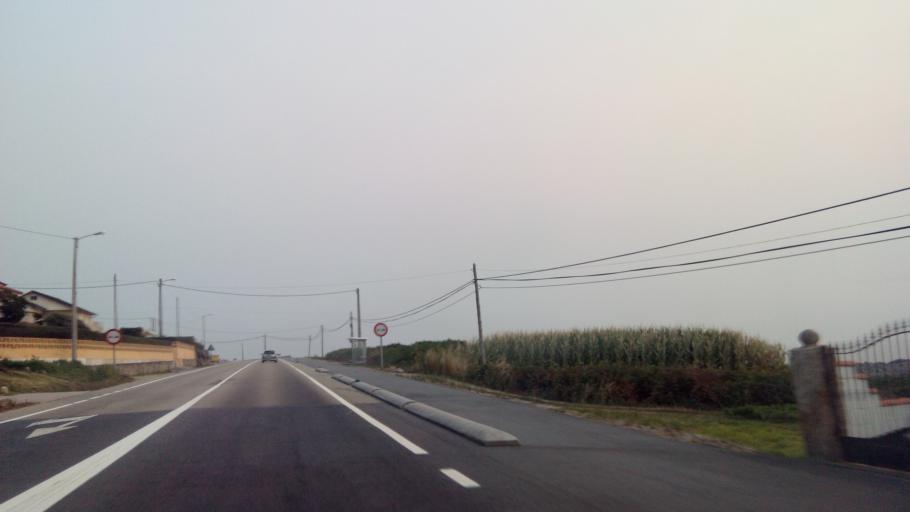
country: ES
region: Galicia
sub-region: Provincia de Pontevedra
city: Oia
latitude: 42.0285
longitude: -8.8840
